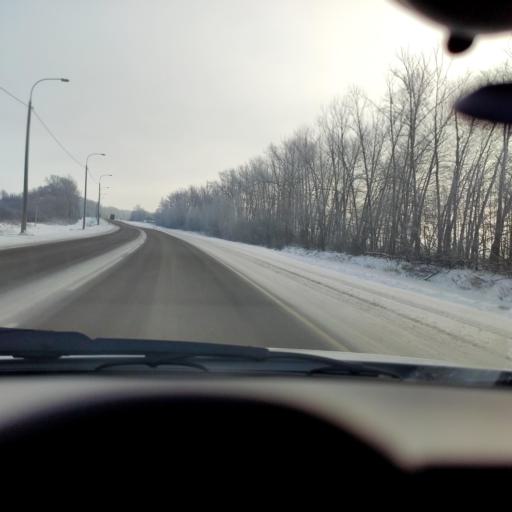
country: RU
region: Kursk
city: Kirovskiy
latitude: 51.6767
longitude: 36.5940
